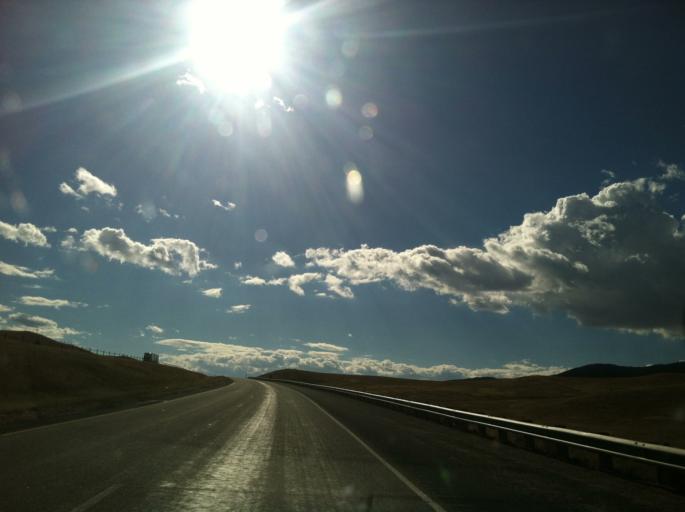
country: US
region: Montana
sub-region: Jefferson County
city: Whitehall
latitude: 45.8930
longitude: -111.8504
